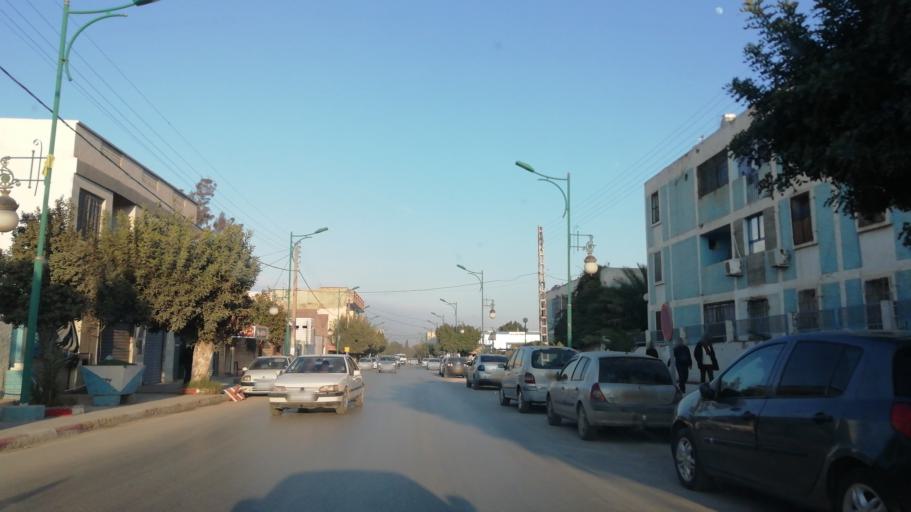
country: DZ
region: Relizane
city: Oued Rhiou
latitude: 35.9643
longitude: 0.9234
